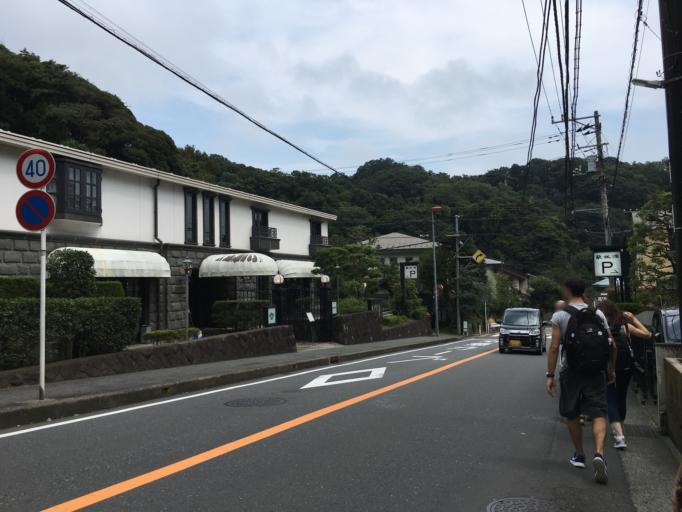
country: JP
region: Kanagawa
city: Kamakura
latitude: 35.3283
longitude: 139.5554
